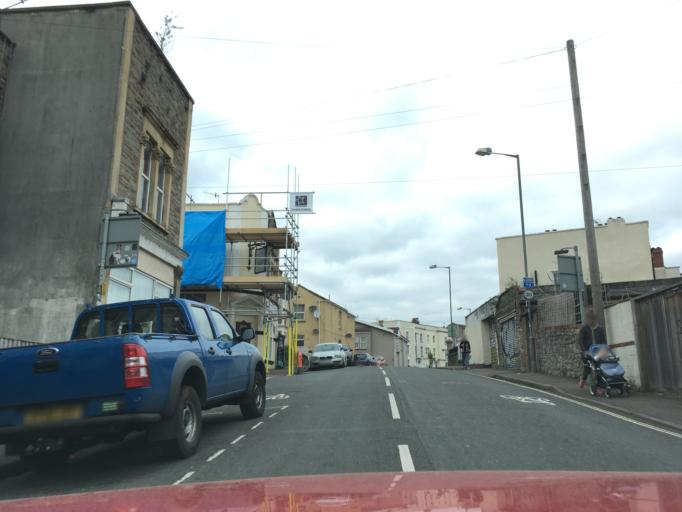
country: GB
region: England
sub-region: Bristol
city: Bristol
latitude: 51.4441
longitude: -2.5999
